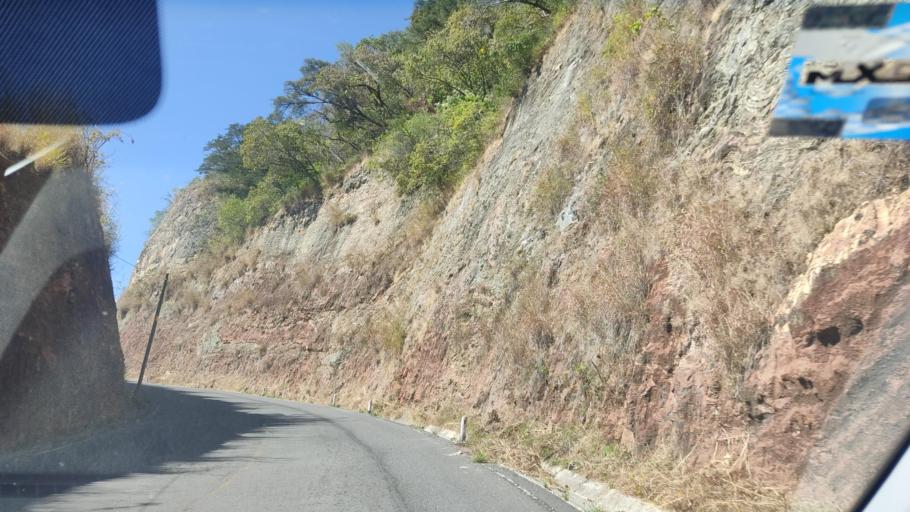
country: MX
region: Nayarit
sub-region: Jala
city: Rosa Blanca
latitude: 21.0912
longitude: -104.3787
